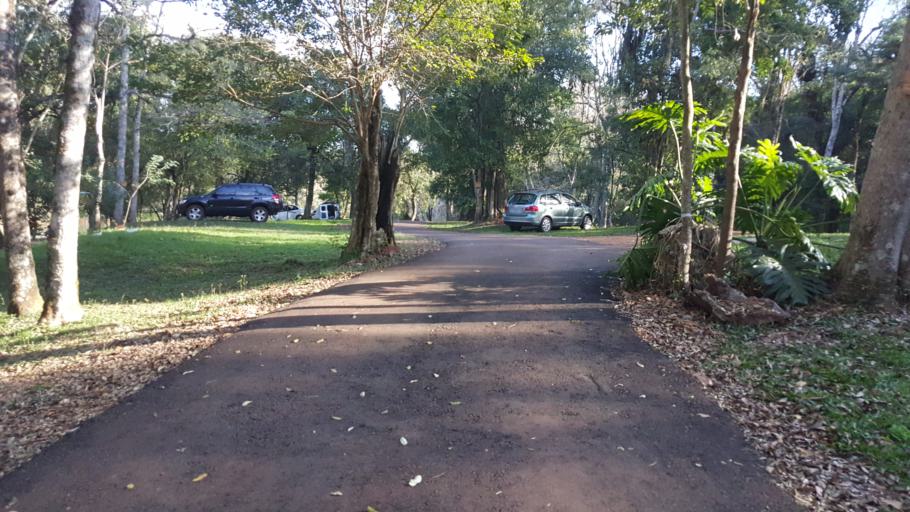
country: AR
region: Misiones
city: Puerto Leoni
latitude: -27.0008
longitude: -55.1791
